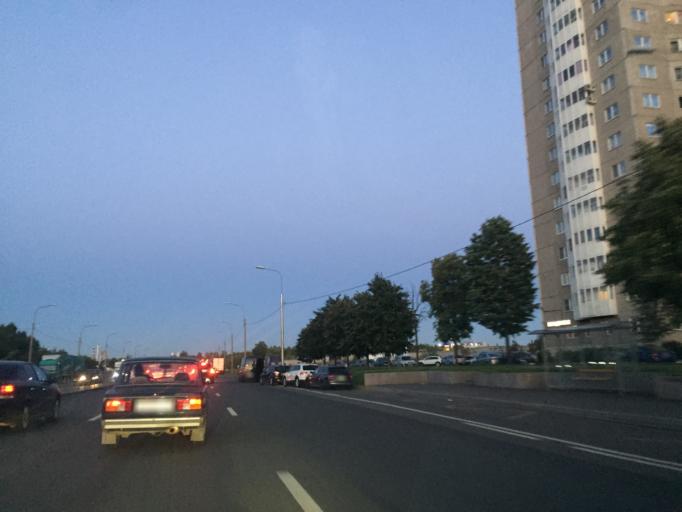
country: RU
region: St.-Petersburg
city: Obukhovo
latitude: 59.8518
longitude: 30.4176
